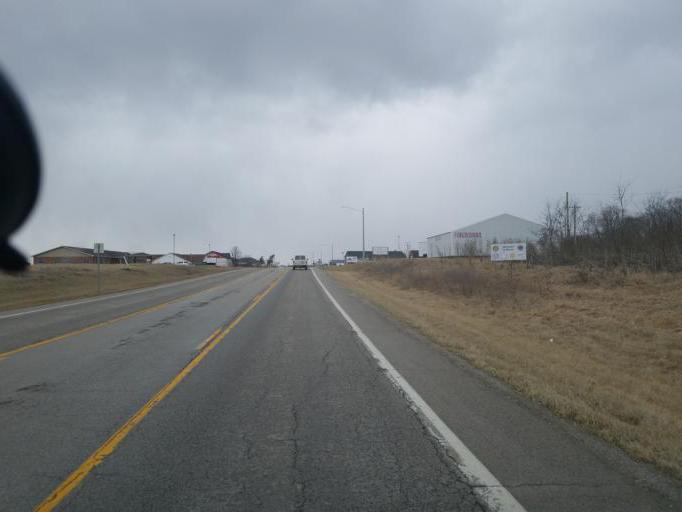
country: US
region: Missouri
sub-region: Macon County
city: Macon
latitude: 39.7626
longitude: -92.4675
